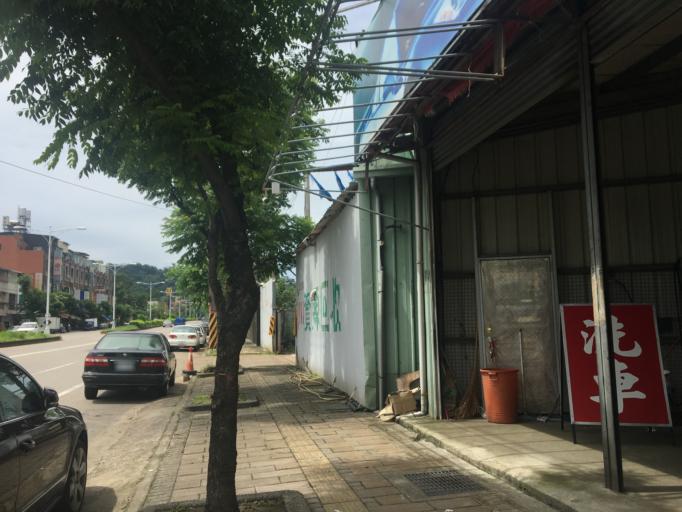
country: TW
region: Taiwan
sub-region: Taichung City
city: Taichung
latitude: 24.0588
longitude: 120.6952
